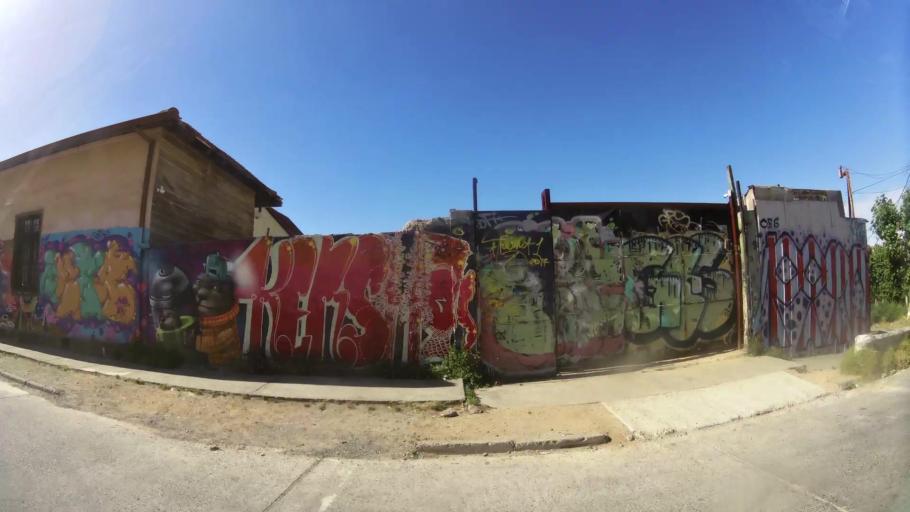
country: CL
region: Valparaiso
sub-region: Provincia de Valparaiso
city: Vina del Mar
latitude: -33.0336
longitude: -71.5671
